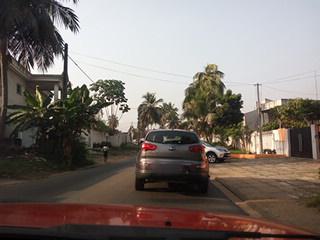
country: CI
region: Lagunes
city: Abobo
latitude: 5.3686
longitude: -3.9914
